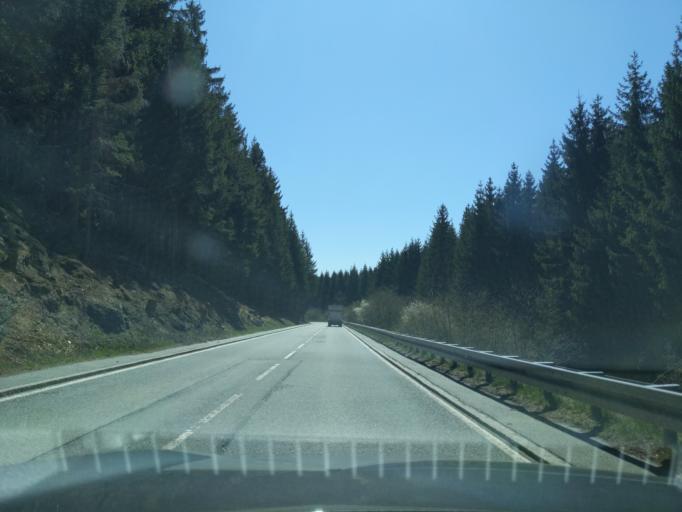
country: DE
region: Saxony
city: Stutzengrun
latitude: 50.5203
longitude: 12.5300
